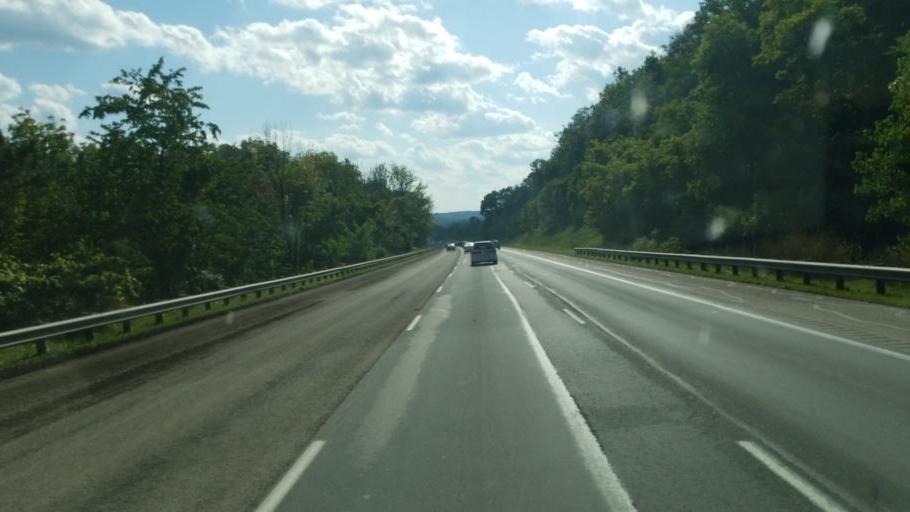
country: US
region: Ohio
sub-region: Ashland County
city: Ashland
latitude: 40.8075
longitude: -82.3746
